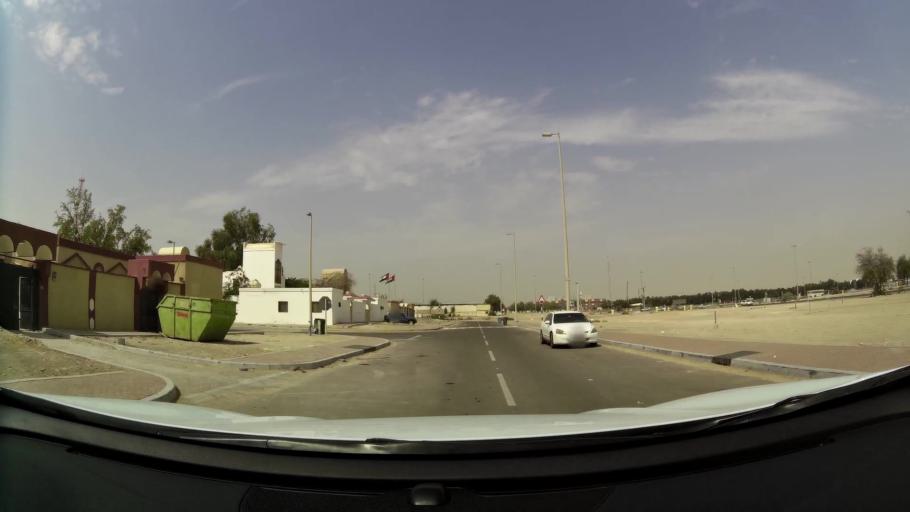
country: AE
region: Abu Dhabi
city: Abu Dhabi
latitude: 24.3134
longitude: 54.6090
